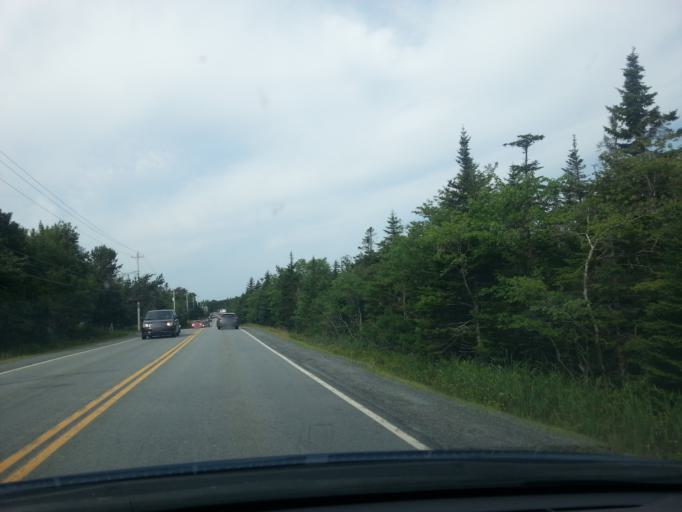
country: CA
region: Nova Scotia
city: Halifax
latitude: 44.5715
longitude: -63.7166
